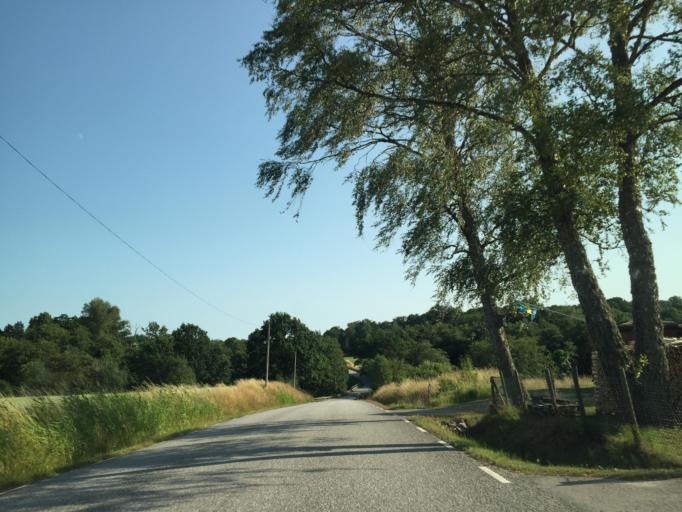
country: SE
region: Vaestra Goetaland
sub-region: Lilla Edets Kommun
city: Lilla Edet
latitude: 58.1886
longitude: 12.1174
